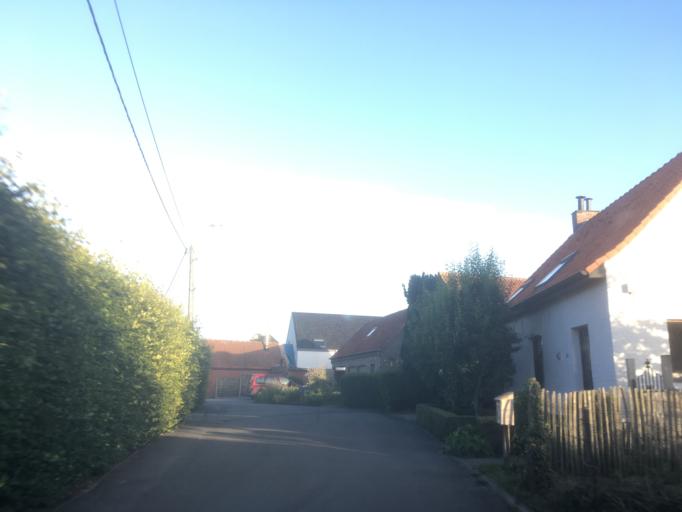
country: BE
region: Flanders
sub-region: Provincie West-Vlaanderen
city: Ichtegem
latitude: 51.0878
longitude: 3.0442
